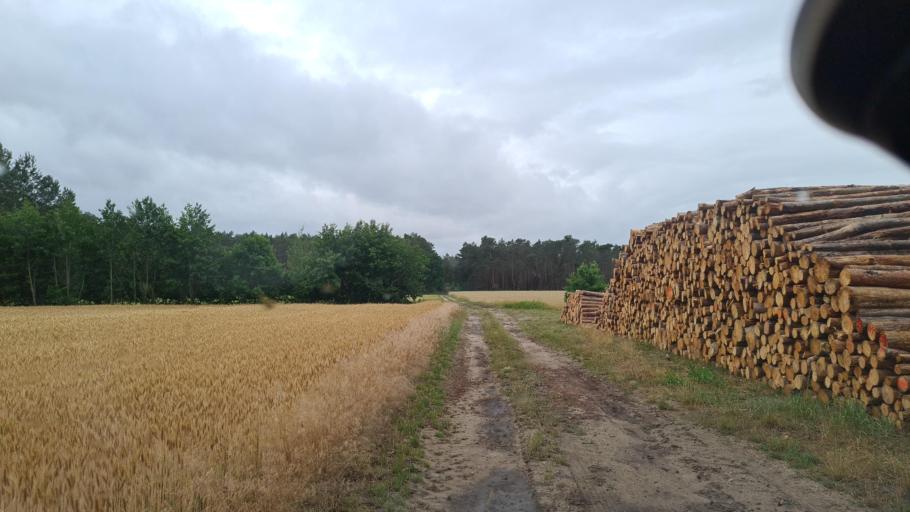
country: DE
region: Saxony-Anhalt
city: Holzdorf
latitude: 51.7869
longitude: 13.1995
